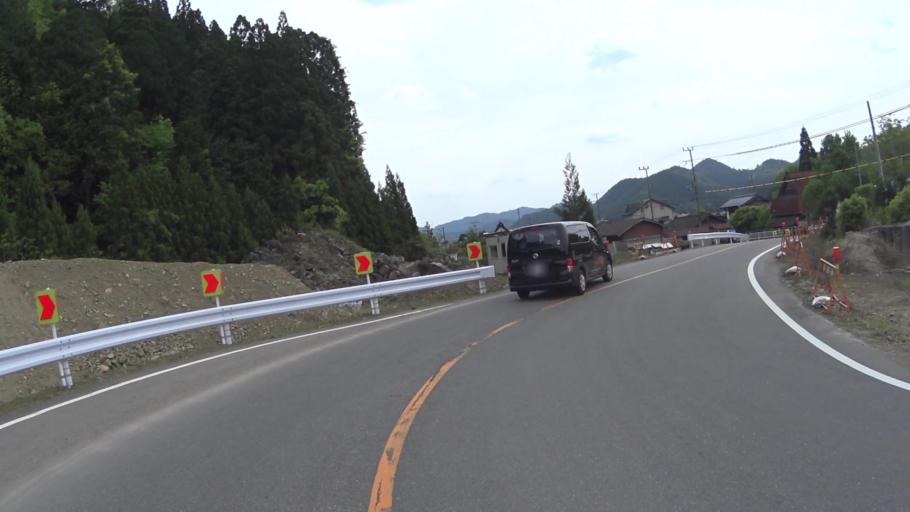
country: JP
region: Kyoto
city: Kameoka
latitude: 35.1921
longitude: 135.6374
